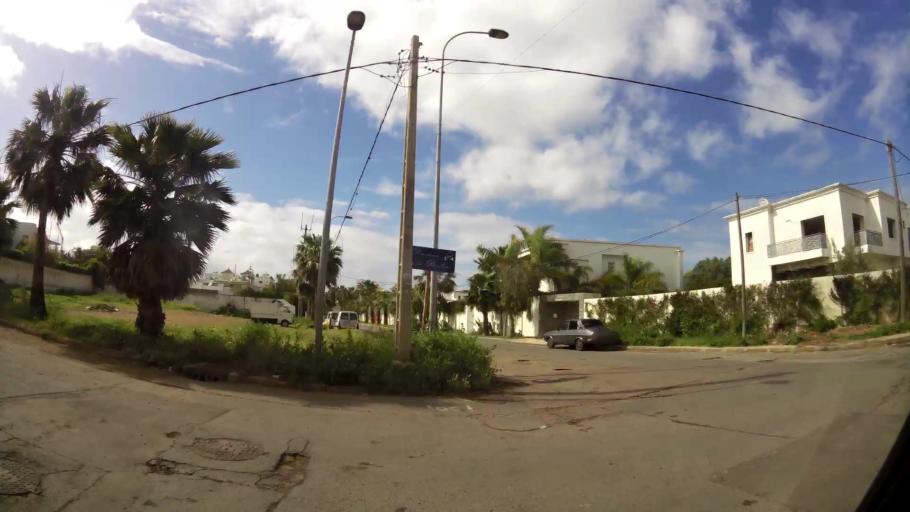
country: MA
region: Grand Casablanca
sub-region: Casablanca
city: Casablanca
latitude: 33.5715
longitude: -7.7052
